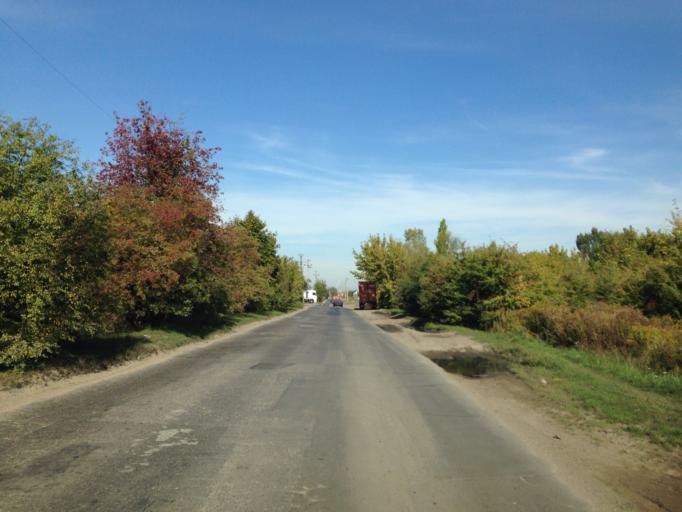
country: PL
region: Masovian Voivodeship
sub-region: Powiat pruszkowski
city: Pruszkow
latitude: 52.1701
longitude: 20.7696
